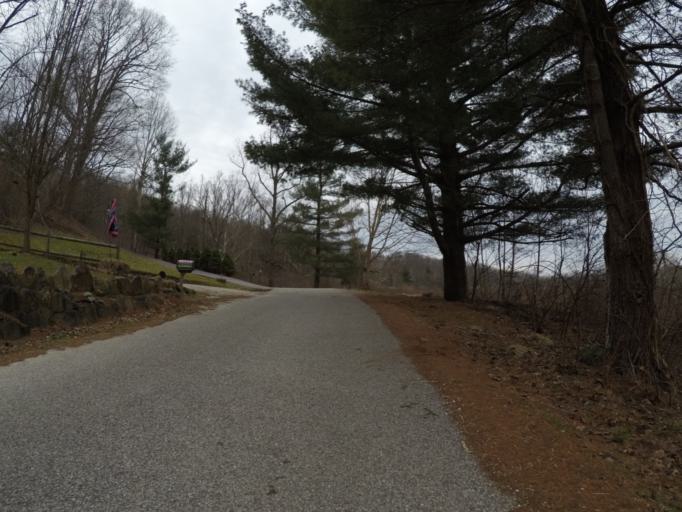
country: US
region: Ohio
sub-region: Lawrence County
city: Burlington
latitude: 38.3822
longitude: -82.5064
